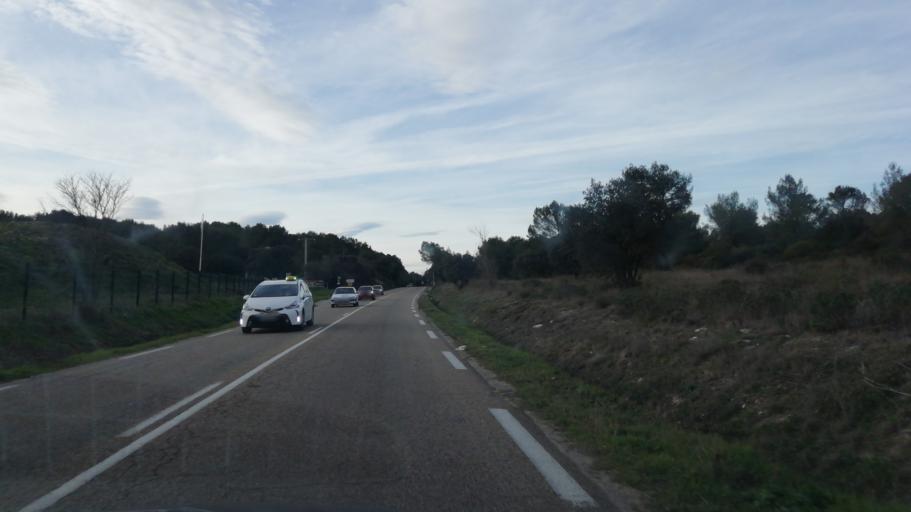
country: FR
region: Languedoc-Roussillon
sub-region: Departement du Gard
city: Caveirac
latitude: 43.8458
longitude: 4.2971
